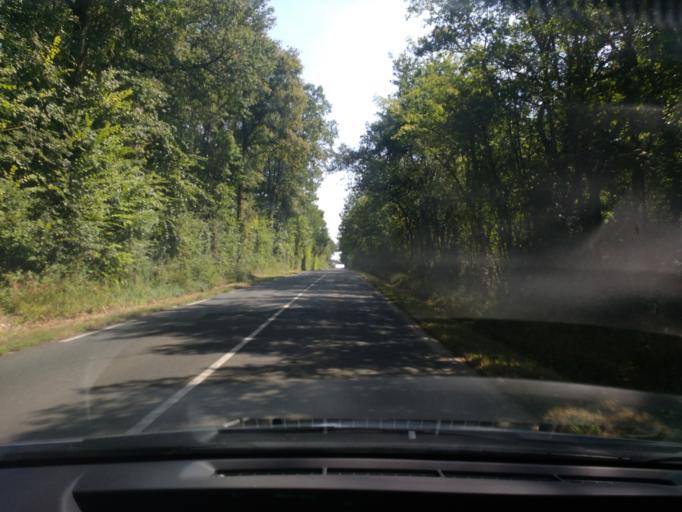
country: FR
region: Pays de la Loire
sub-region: Departement de Maine-et-Loire
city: Trelaze
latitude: 47.4686
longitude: -0.4694
